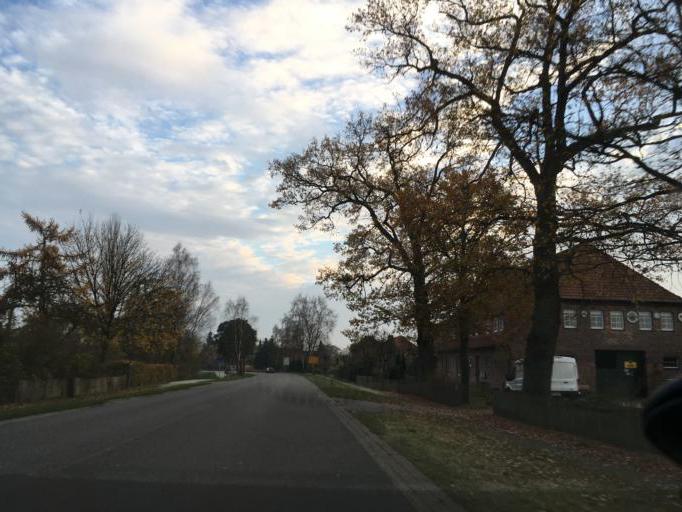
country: DE
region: Lower Saxony
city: Hambuhren
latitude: 52.6993
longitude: 9.9814
